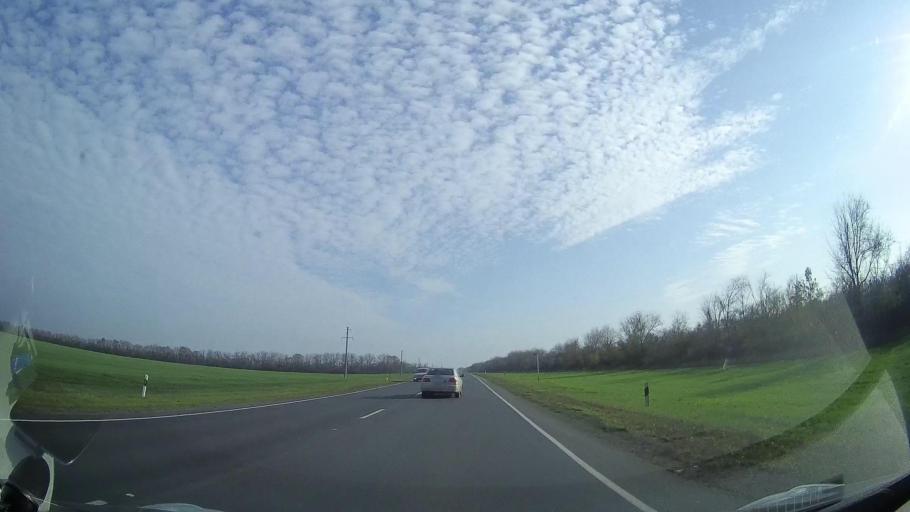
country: RU
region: Rostov
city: Gigant
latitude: 46.5285
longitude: 41.1990
